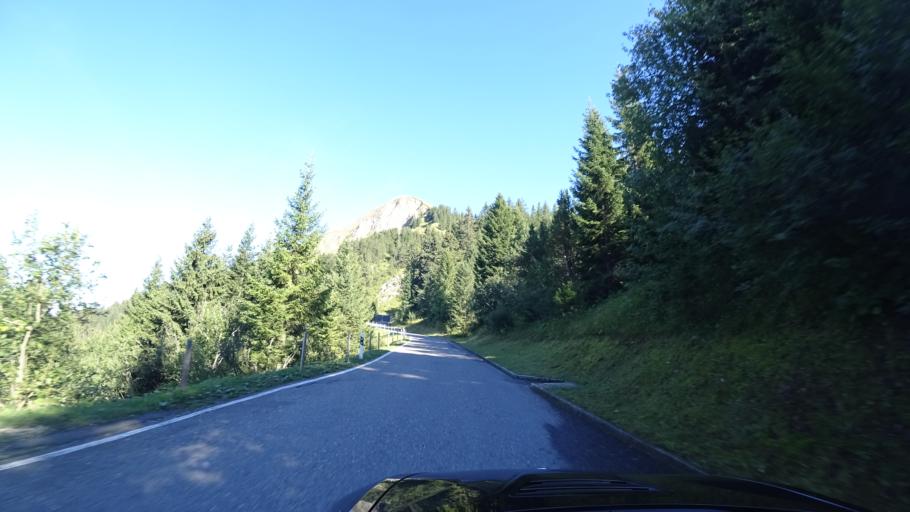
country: CH
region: Obwalden
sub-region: Obwalden
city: Lungern
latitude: 46.8180
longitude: 8.0882
